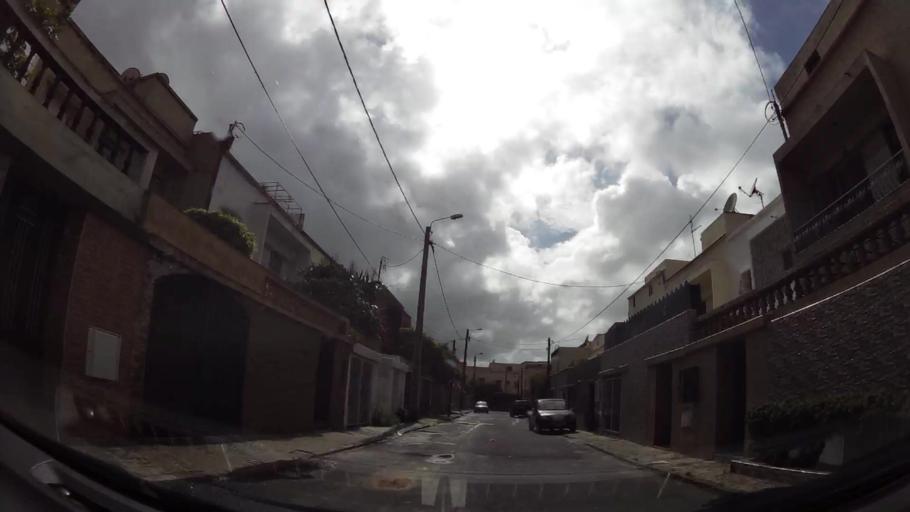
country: MA
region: Grand Casablanca
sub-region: Casablanca
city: Casablanca
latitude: 33.5550
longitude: -7.6061
